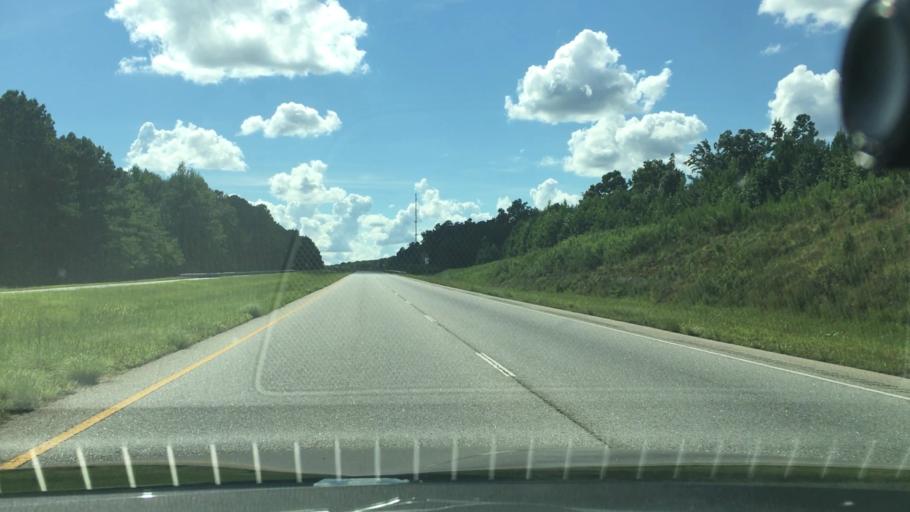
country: US
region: Georgia
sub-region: Spalding County
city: East Griffin
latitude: 33.2377
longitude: -84.1959
